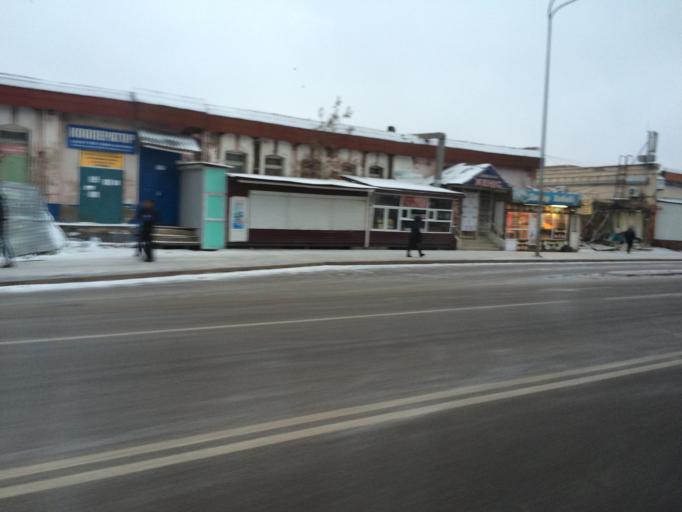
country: KZ
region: Astana Qalasy
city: Astana
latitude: 51.1749
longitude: 71.4377
